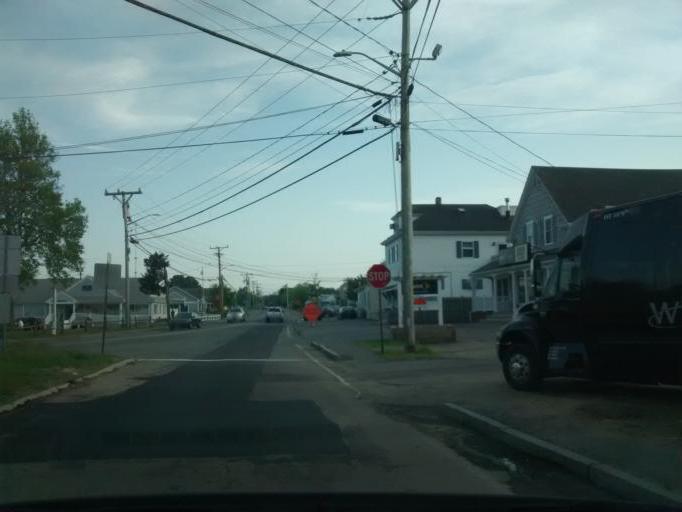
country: US
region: Massachusetts
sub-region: Barnstable County
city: Teaticket
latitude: 41.5686
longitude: -70.5947
